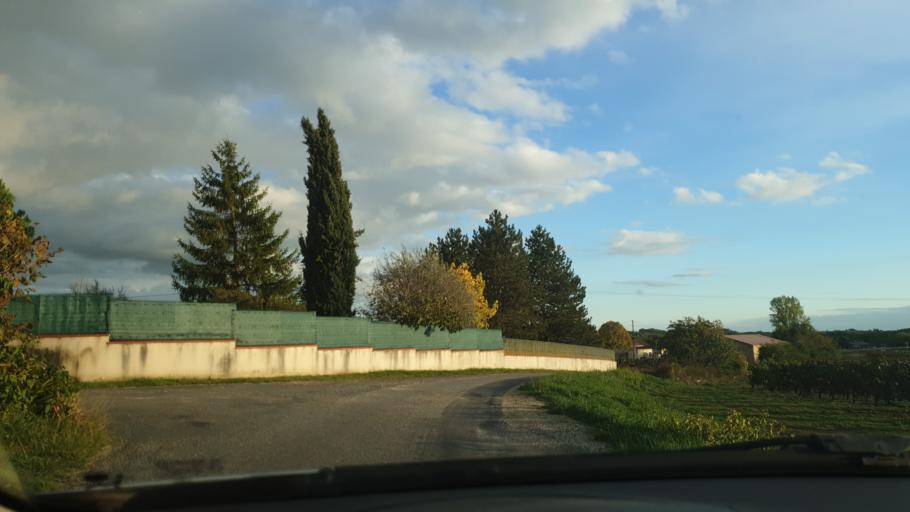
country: FR
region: Midi-Pyrenees
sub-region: Departement du Lot
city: Luzech
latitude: 44.4148
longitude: 1.2526
